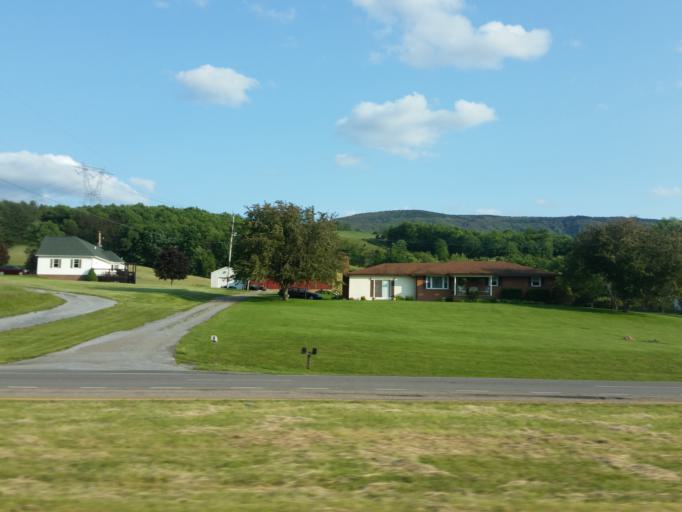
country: US
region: Virginia
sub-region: Russell County
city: Honaker
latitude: 36.9748
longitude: -81.8882
